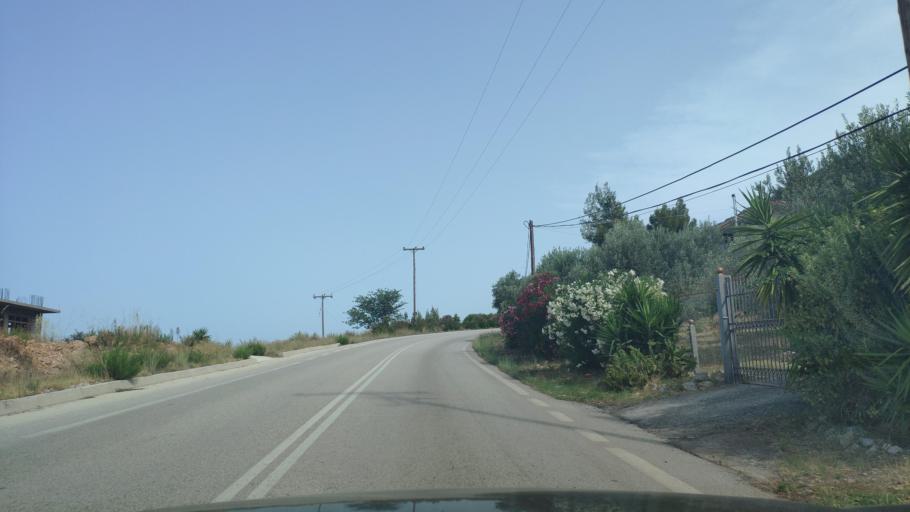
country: GR
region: Peloponnese
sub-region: Nomos Argolidos
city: Palaia Epidavros
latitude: 37.6305
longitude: 23.1397
